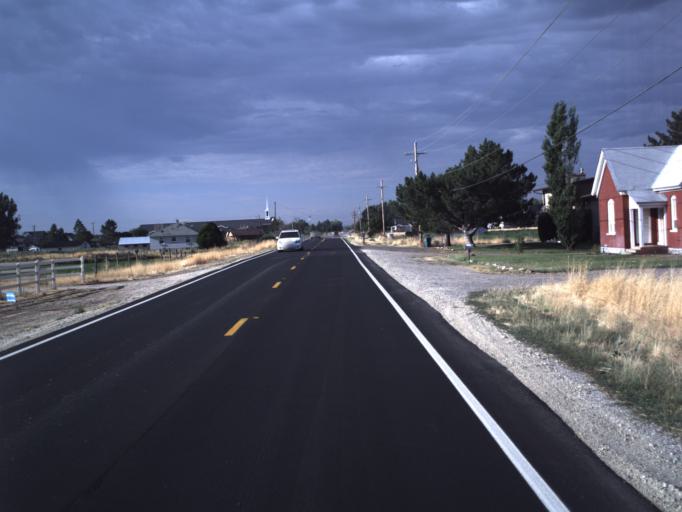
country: US
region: Utah
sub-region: Weber County
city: West Haven
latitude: 41.2092
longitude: -112.0930
